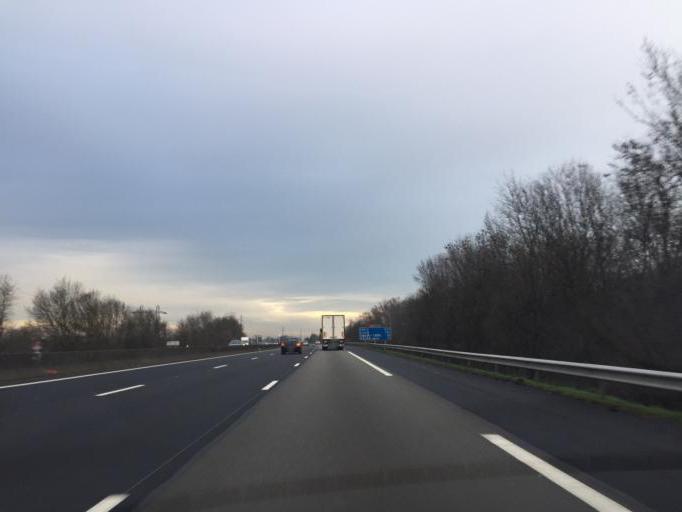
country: FR
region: Rhone-Alpes
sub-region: Departement du Rhone
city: Belleville
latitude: 46.1072
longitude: 4.7577
